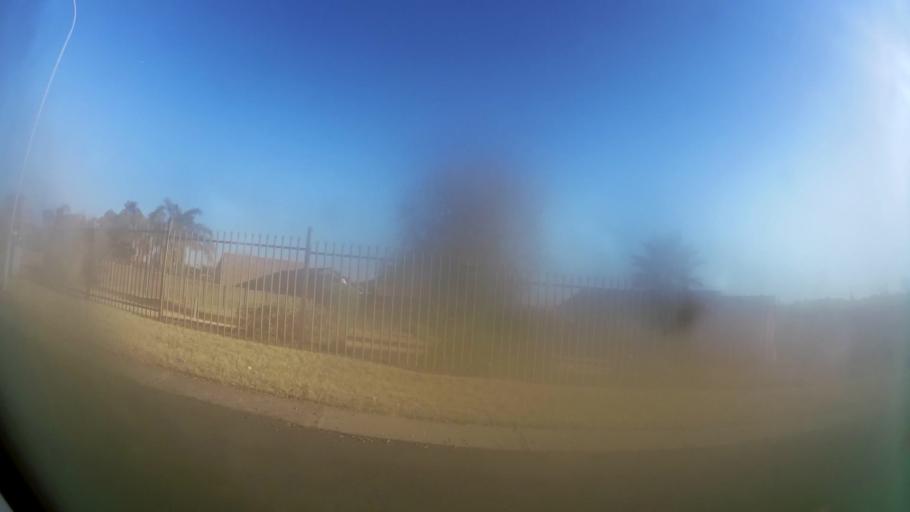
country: ZA
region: Gauteng
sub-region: City of Tshwane Metropolitan Municipality
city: Centurion
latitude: -25.9059
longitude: 28.1309
